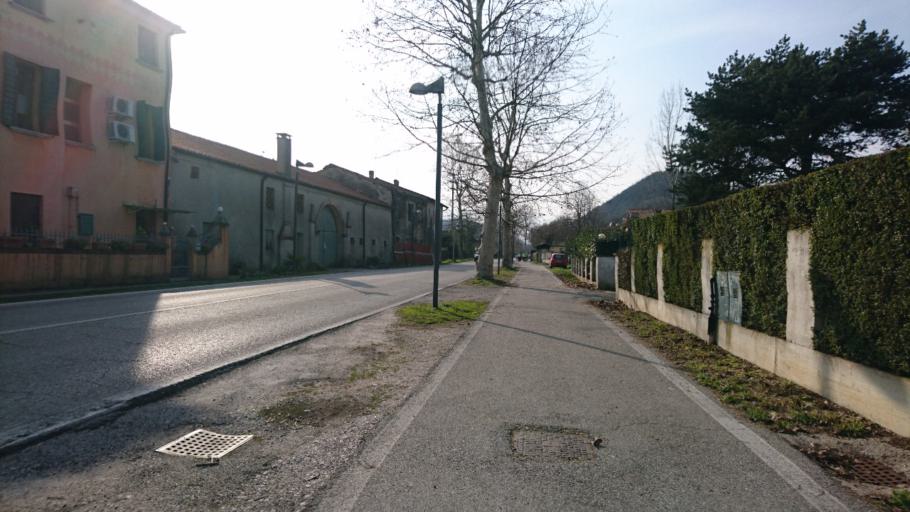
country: IT
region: Veneto
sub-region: Provincia di Padova
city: Abano Terme
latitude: 45.3656
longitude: 11.7660
